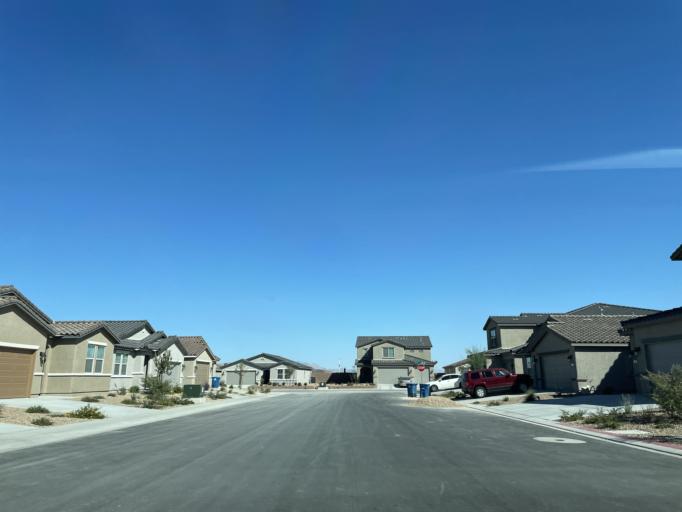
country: US
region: Nevada
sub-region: Nye County
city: Pahrump
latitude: 36.5755
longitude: -115.6651
